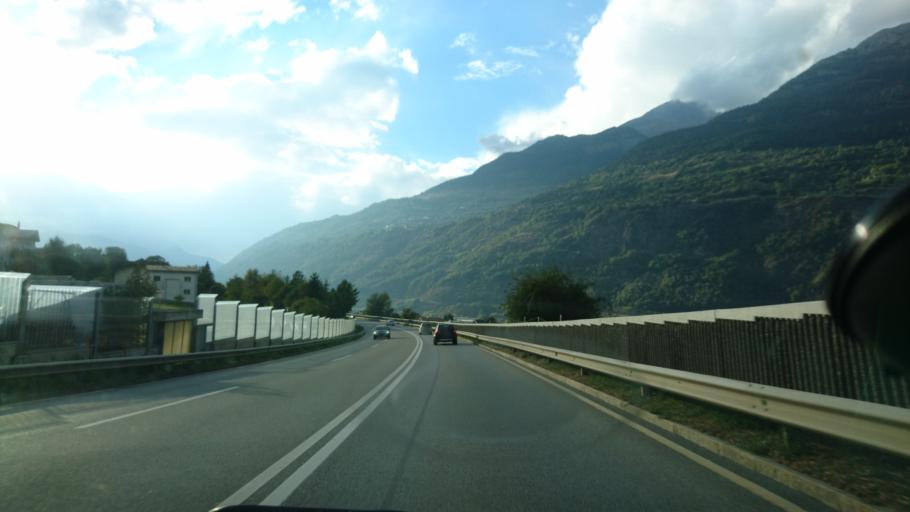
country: CH
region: Valais
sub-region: Brig District
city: Brig
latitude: 46.3086
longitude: 7.9847
